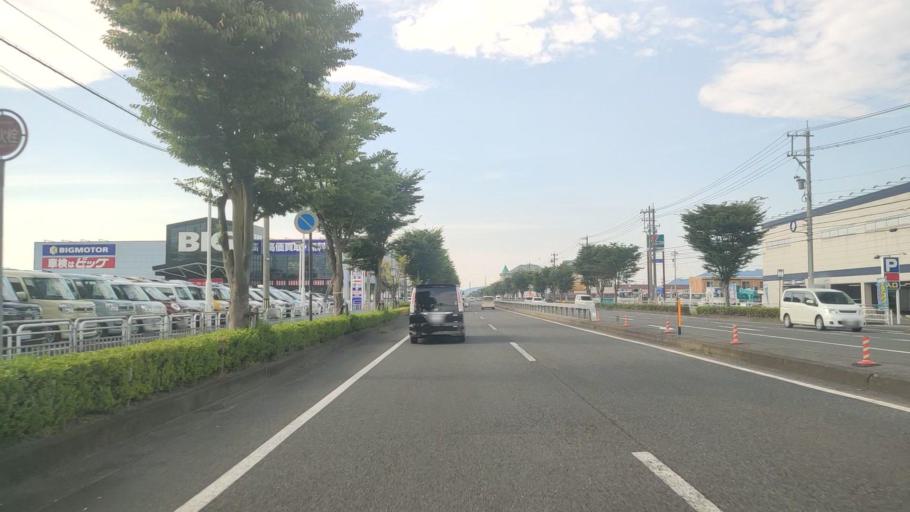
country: JP
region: Fukui
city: Takefu
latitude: 35.9124
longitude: 136.1916
